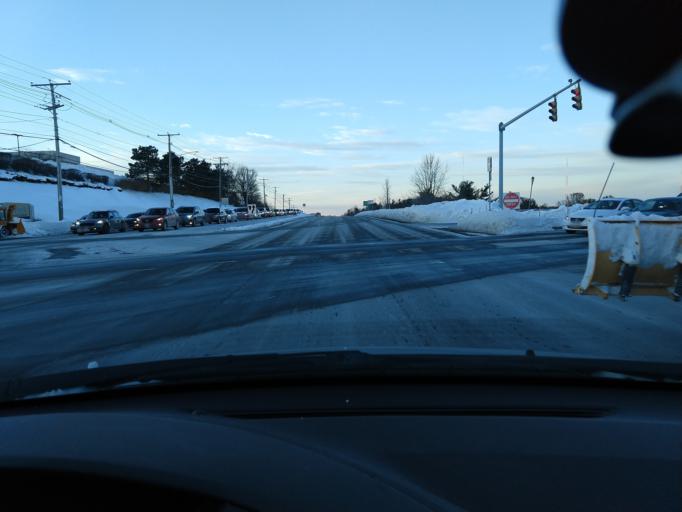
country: US
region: Massachusetts
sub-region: Middlesex County
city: Burlington
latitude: 42.4809
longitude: -71.2171
